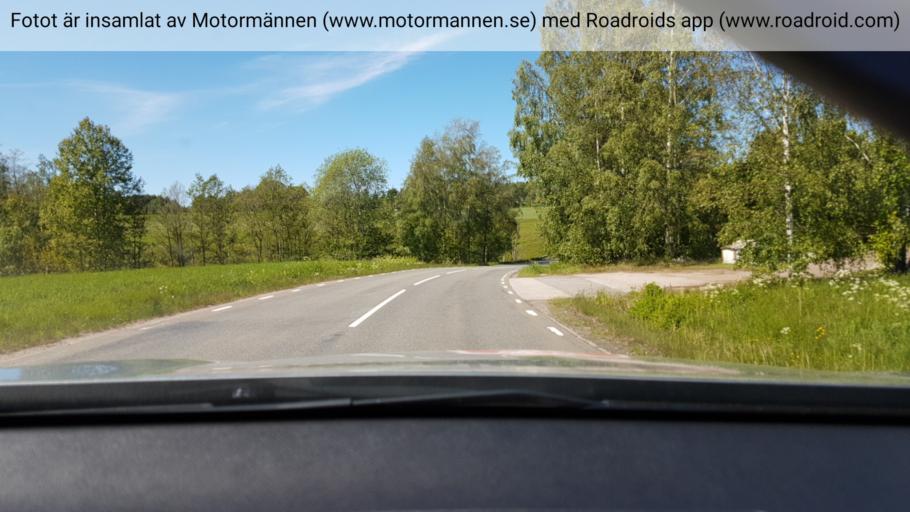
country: SE
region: Vaestra Goetaland
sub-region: Gullspangs Kommun
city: Hova
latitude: 58.8144
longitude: 14.2359
